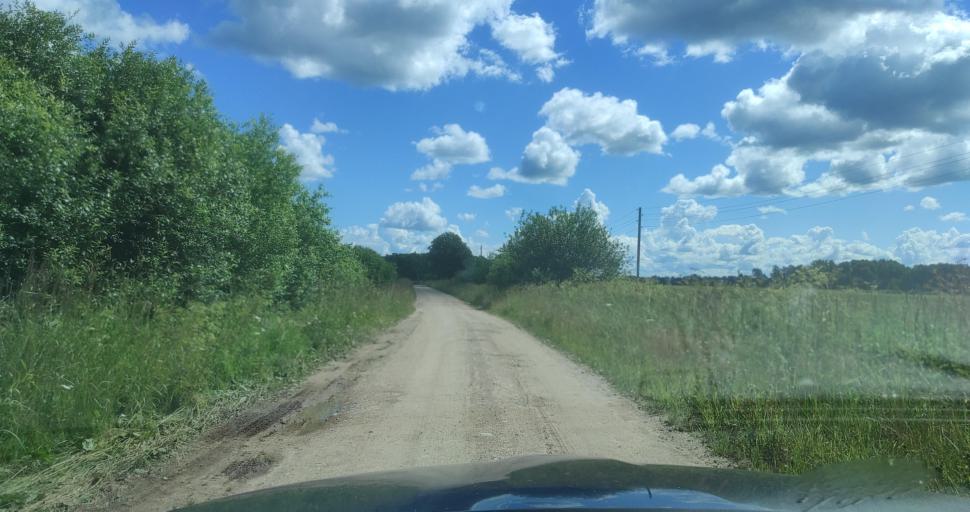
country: LV
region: Kuldigas Rajons
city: Kuldiga
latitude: 57.0015
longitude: 22.1408
